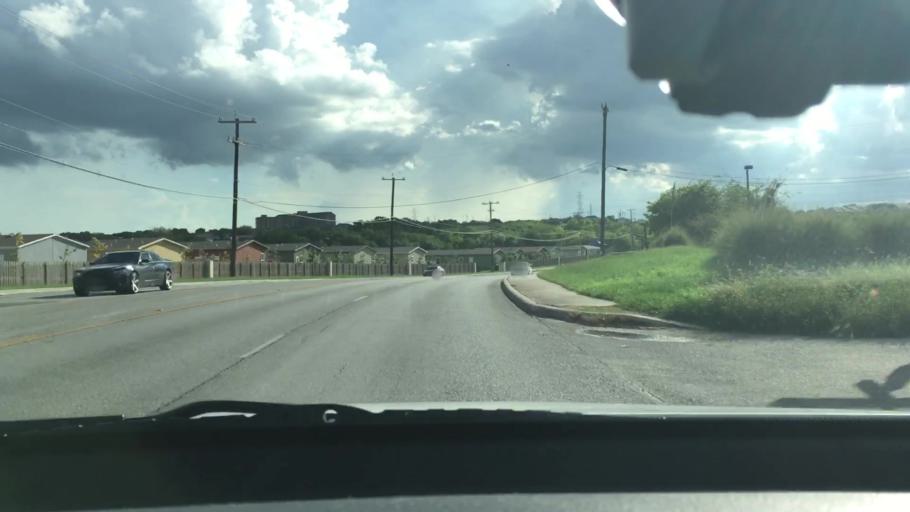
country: US
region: Texas
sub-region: Bexar County
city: Converse
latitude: 29.5280
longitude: -98.3381
